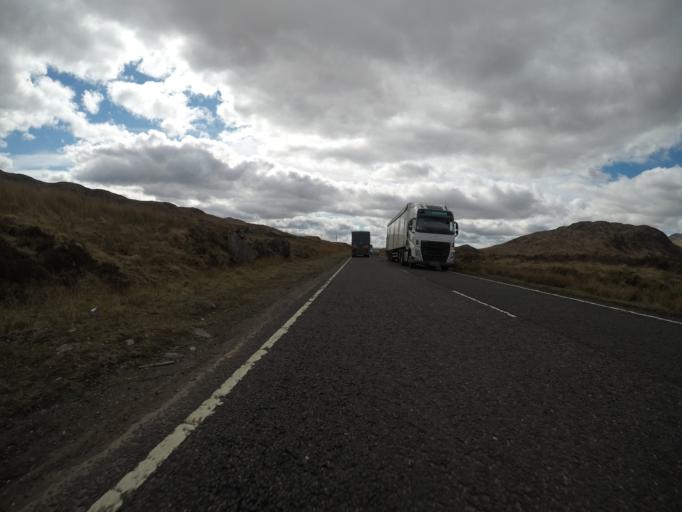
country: GB
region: Scotland
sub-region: Highland
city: Spean Bridge
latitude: 56.5920
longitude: -4.7448
